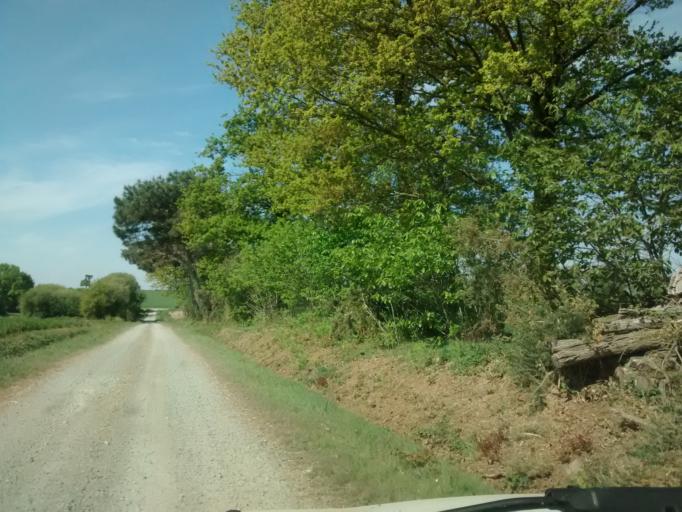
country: FR
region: Brittany
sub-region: Departement d'Ille-et-Vilaine
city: Grand-Fougeray
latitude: 47.7828
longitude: -1.7525
